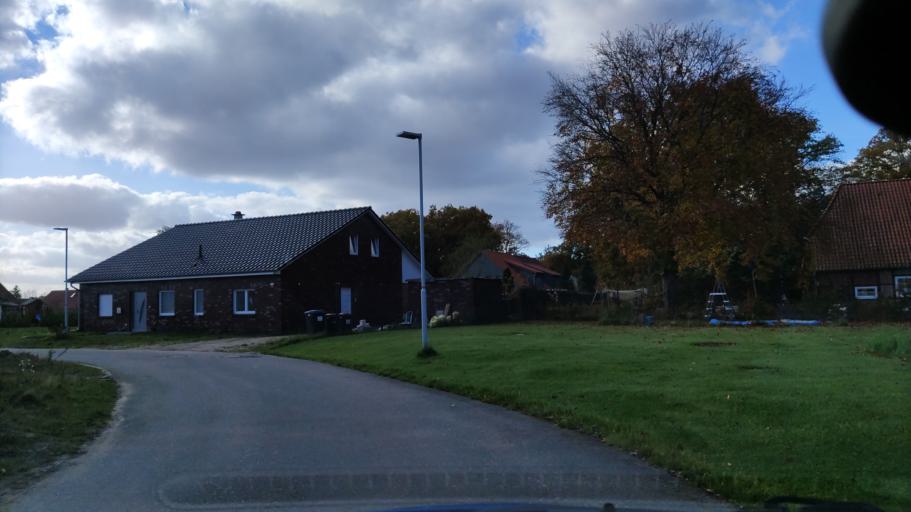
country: DE
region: Lower Saxony
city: Munster
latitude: 53.0153
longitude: 10.0880
